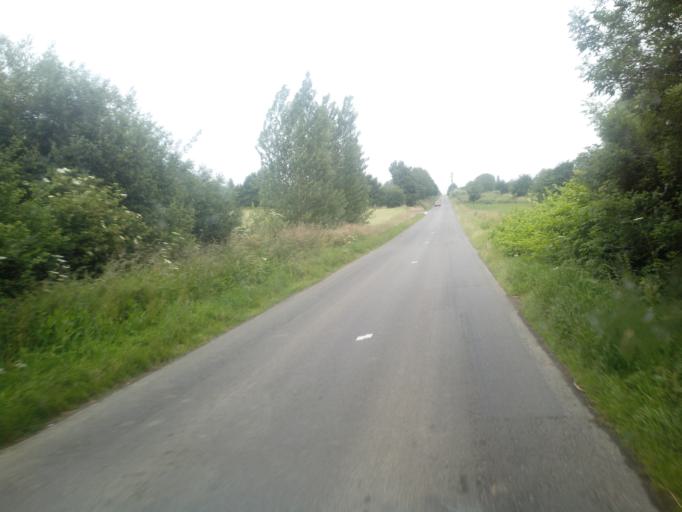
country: FR
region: Brittany
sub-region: Departement d'Ille-et-Vilaine
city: Chevaigne
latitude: 48.2472
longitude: -1.6294
